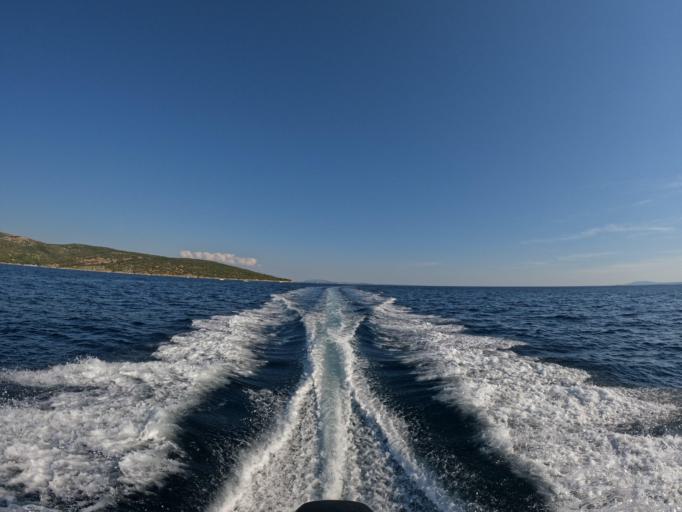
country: HR
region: Primorsko-Goranska
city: Punat
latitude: 44.9915
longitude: 14.6053
